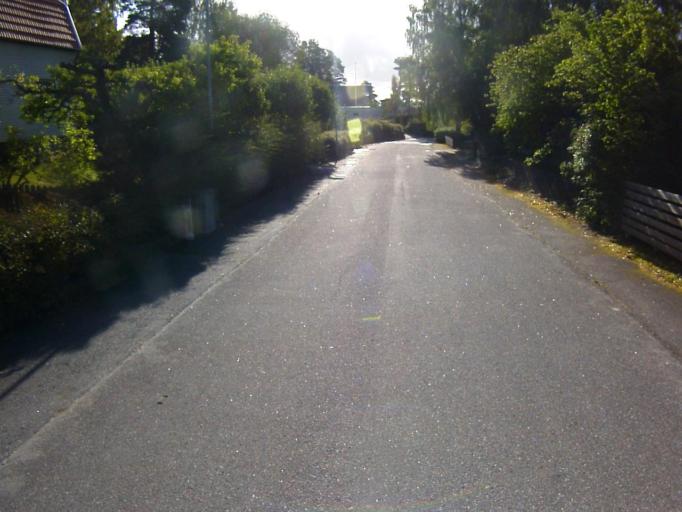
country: SE
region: Soedermanland
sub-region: Eskilstuna Kommun
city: Eskilstuna
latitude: 59.3792
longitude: 16.5520
